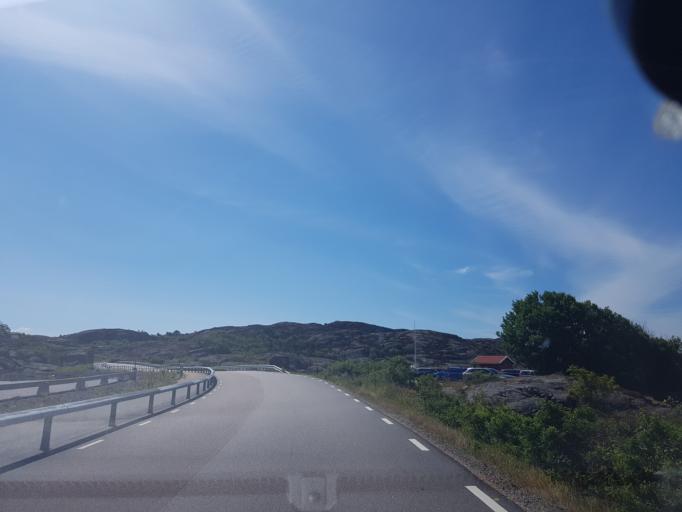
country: SE
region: Vaestra Goetaland
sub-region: Lysekils Kommun
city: Lysekil
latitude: 58.1701
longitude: 11.4147
